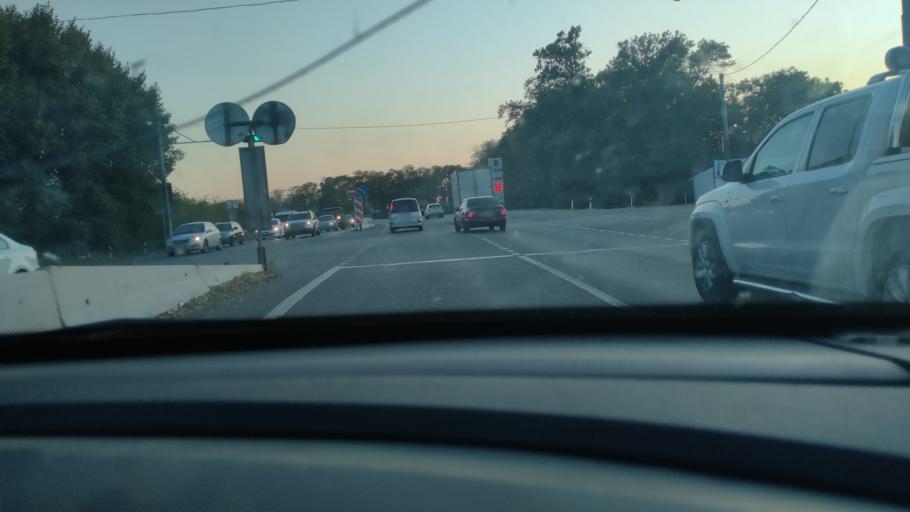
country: RU
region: Krasnodarskiy
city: Timashevsk
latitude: 45.5948
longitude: 38.9202
